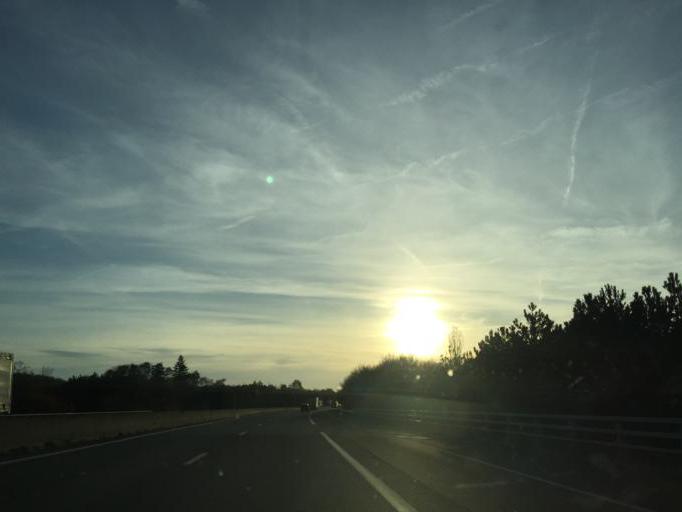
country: FR
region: Rhone-Alpes
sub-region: Departement du Rhone
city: Communay
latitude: 45.5976
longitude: 4.8527
